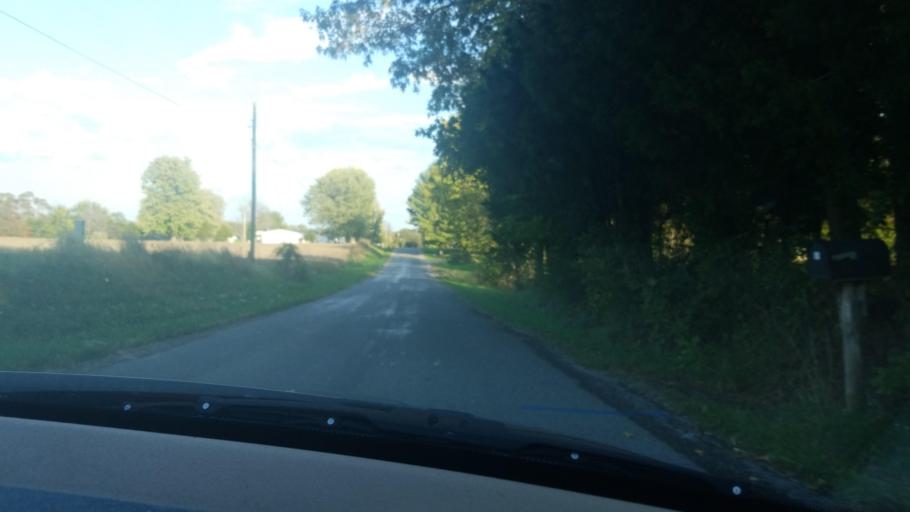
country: US
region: Illinois
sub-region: Williamson County
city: Marion
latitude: 37.7610
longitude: -88.7945
